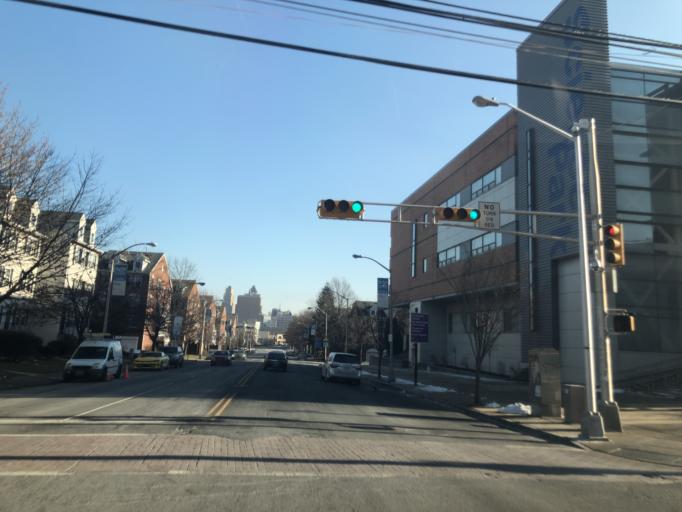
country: US
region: New Jersey
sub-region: Essex County
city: Newark
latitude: 40.7409
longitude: -74.1856
